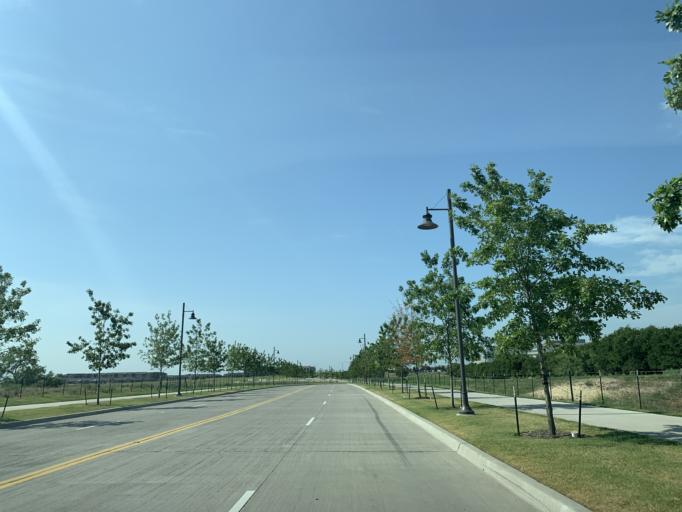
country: US
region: Texas
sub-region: Tarrant County
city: Haslet
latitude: 32.9269
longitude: -97.3127
